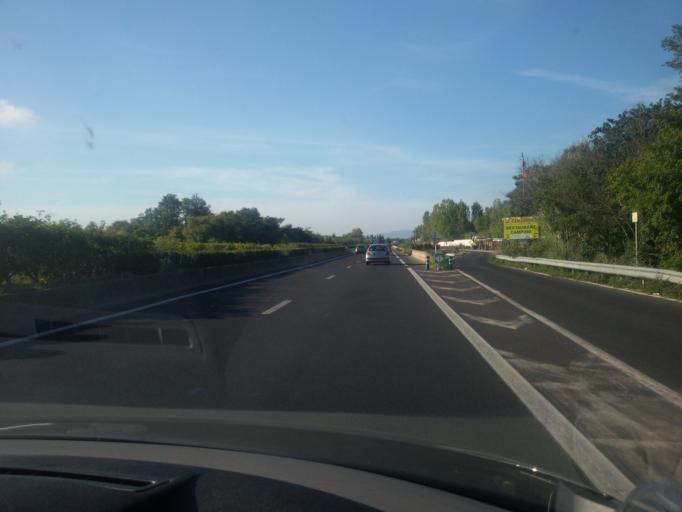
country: FR
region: Languedoc-Roussillon
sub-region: Departement de l'Herault
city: Lattes
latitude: 43.5472
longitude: 3.8950
